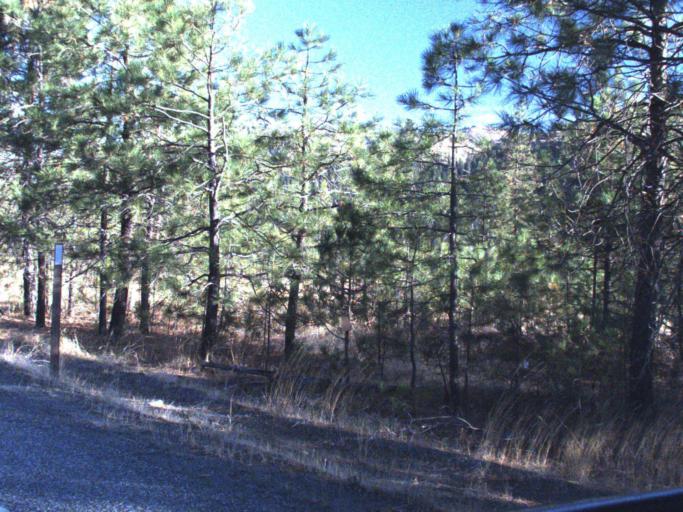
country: US
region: Washington
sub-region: Okanogan County
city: Coulee Dam
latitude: 48.0942
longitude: -118.6922
